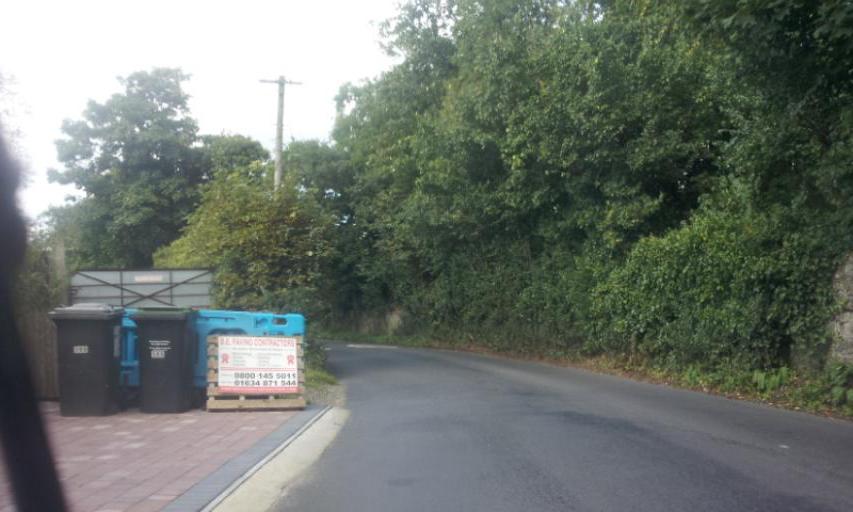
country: GB
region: England
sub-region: Kent
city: Larkfield
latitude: 51.2935
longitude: 0.4269
